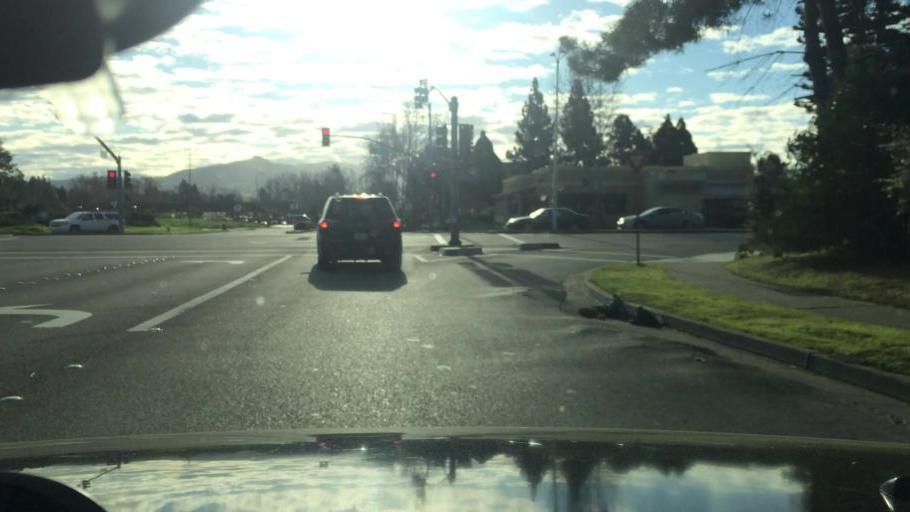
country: US
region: California
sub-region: Alameda County
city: Fremont
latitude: 37.5535
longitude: -121.9855
